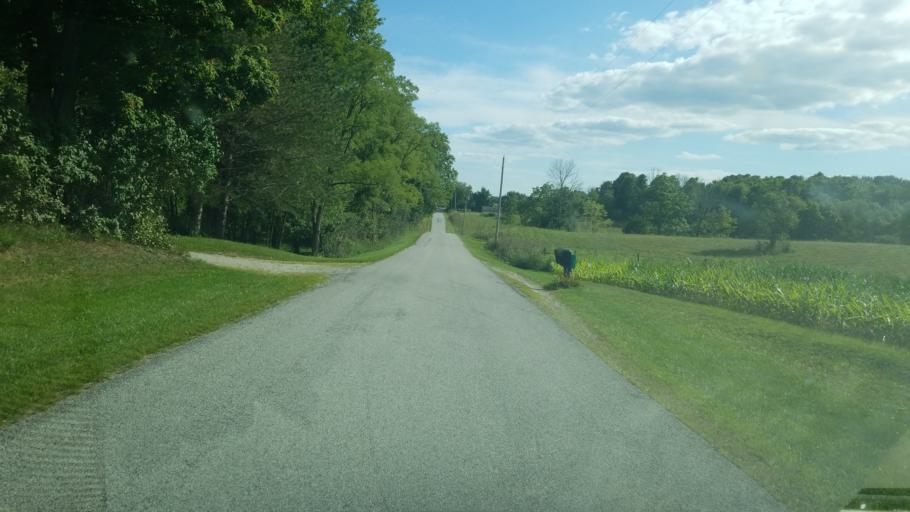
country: US
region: Ohio
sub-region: Champaign County
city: Saint Paris
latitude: 40.1381
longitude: -83.8731
